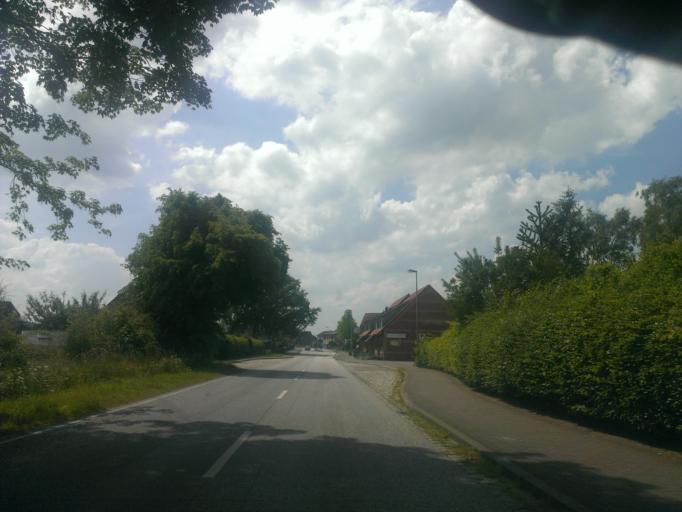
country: DE
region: Schleswig-Holstein
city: Elsdorf-Westermuhlen
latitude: 54.2582
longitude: 9.5359
